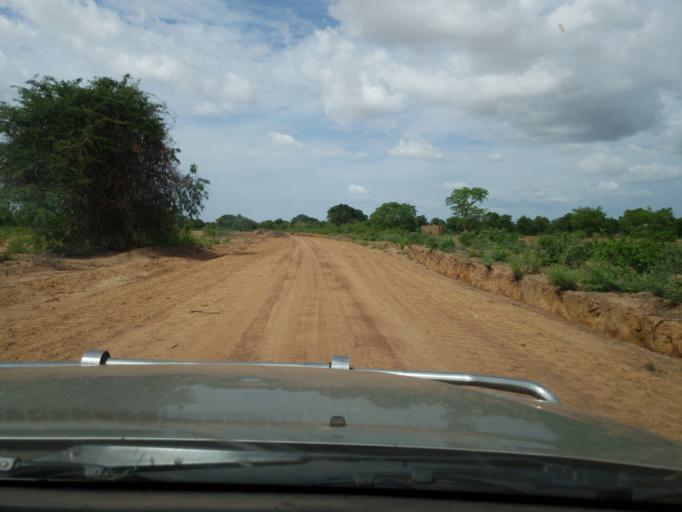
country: ML
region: Segou
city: Bla
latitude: 12.7109
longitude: -5.6894
